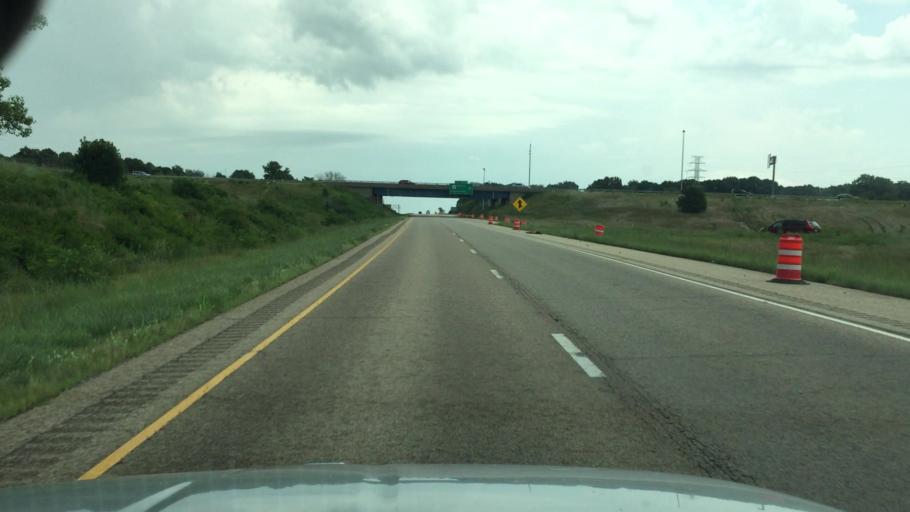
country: US
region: Illinois
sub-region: Peoria County
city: Bellevue
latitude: 40.7419
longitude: -89.6705
